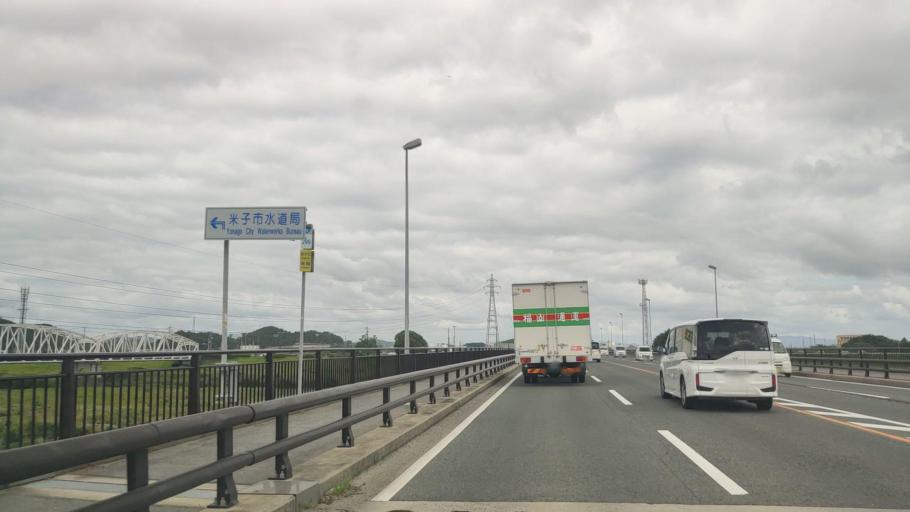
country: JP
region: Tottori
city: Yonago
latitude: 35.4311
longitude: 133.3675
